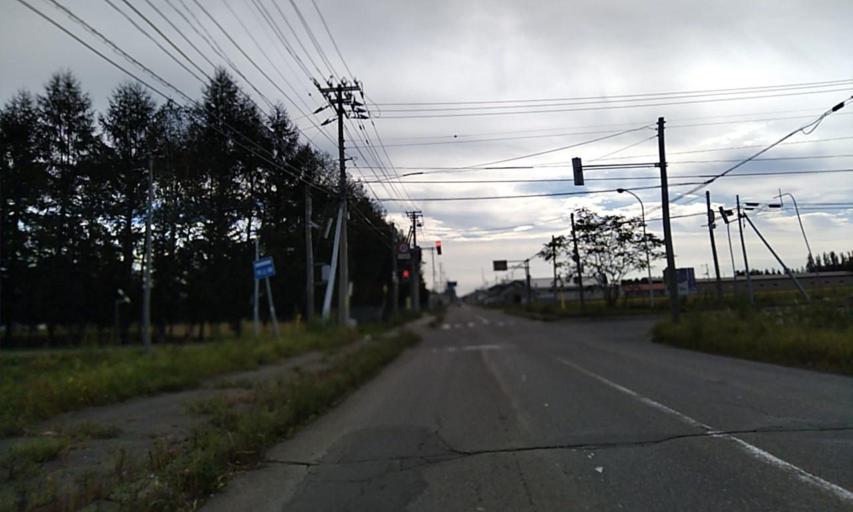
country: JP
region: Hokkaido
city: Obihiro
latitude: 42.8514
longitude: 143.1611
